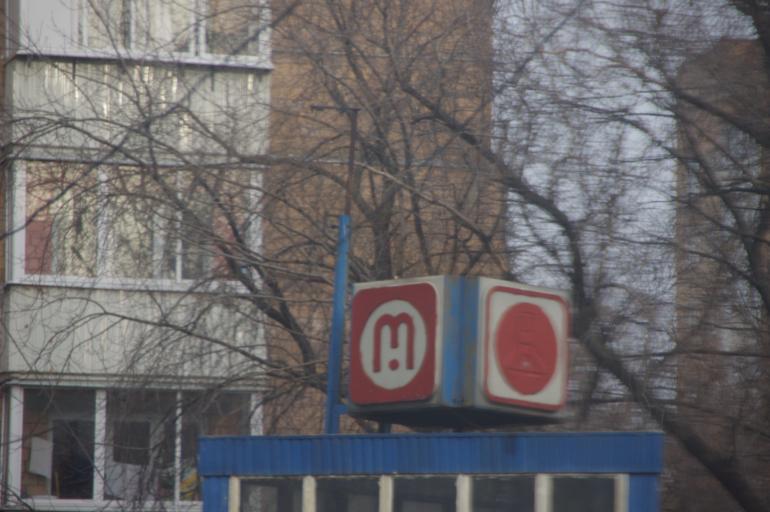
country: RU
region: Moscow
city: Kolomenskoye
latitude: 55.6788
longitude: 37.6664
